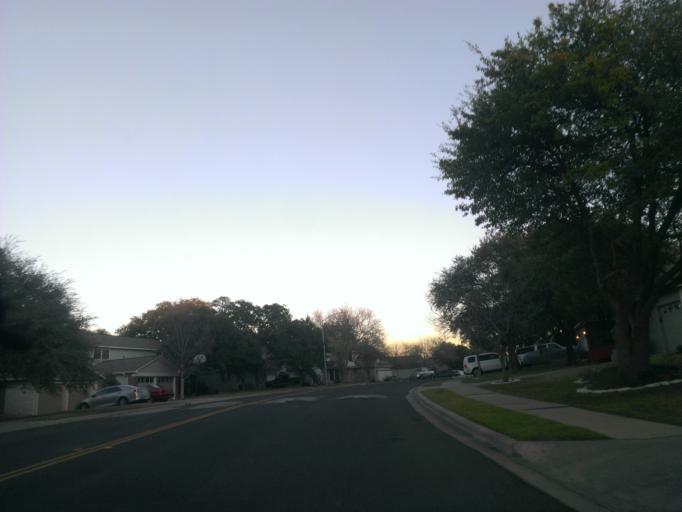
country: US
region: Texas
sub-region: Travis County
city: Wells Branch
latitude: 30.3973
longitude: -97.6986
